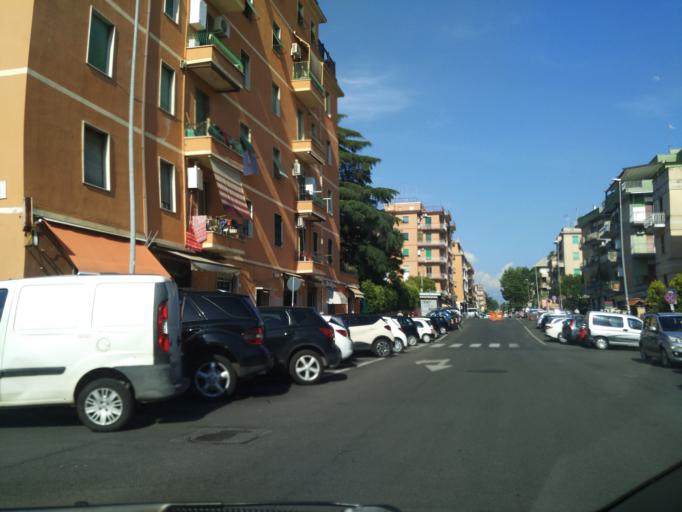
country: IT
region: Latium
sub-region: Citta metropolitana di Roma Capitale
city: Rome
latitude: 41.8813
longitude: 12.5622
